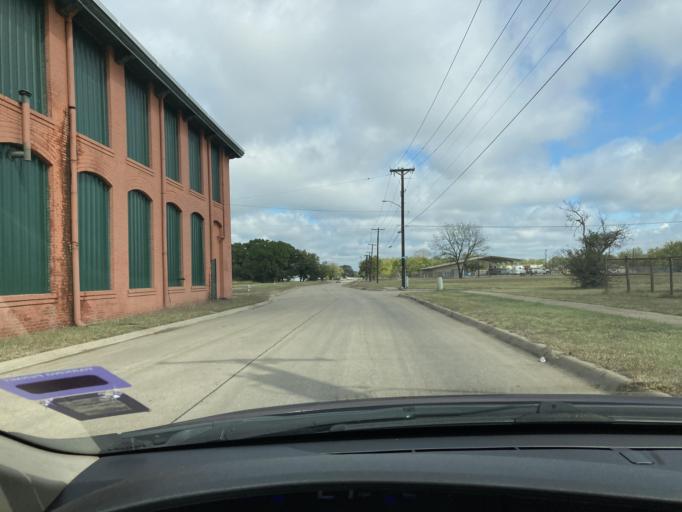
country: US
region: Texas
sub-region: Navarro County
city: Corsicana
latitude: 32.0876
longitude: -96.4606
